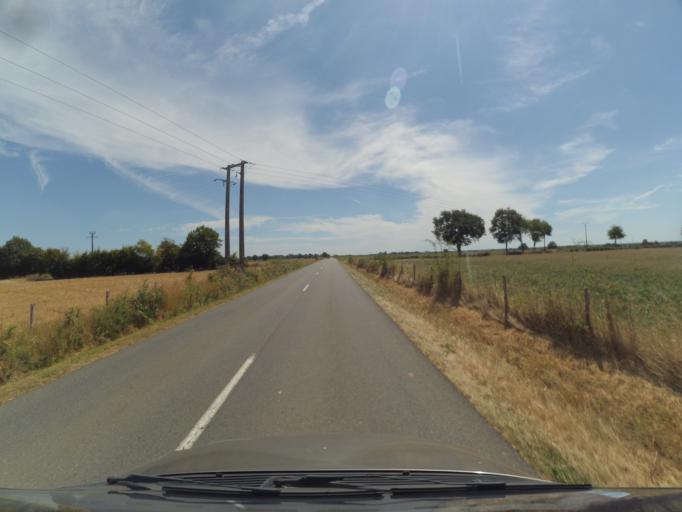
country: FR
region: Poitou-Charentes
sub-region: Departement de la Vienne
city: Usson-du-Poitou
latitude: 46.1862
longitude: 0.5406
